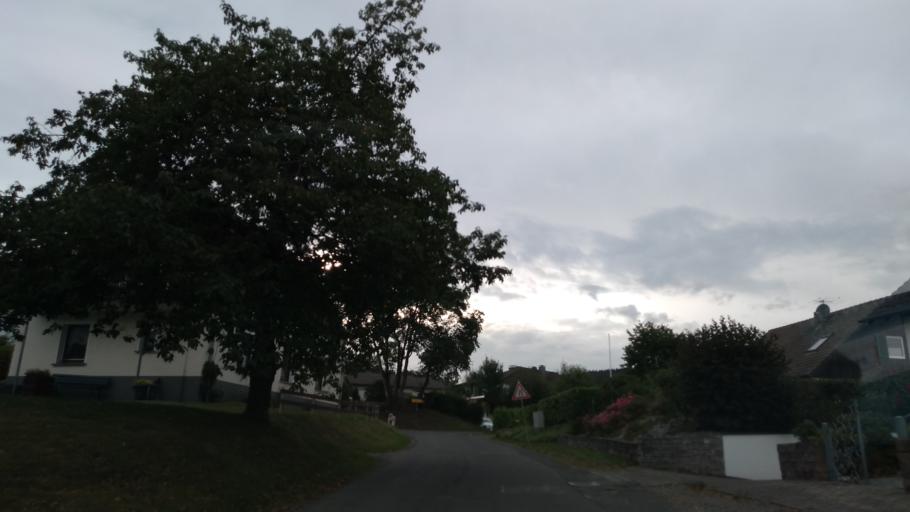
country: DE
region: North Rhine-Westphalia
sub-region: Regierungsbezirk Arnsberg
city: Herscheid
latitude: 51.1917
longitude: 7.7751
